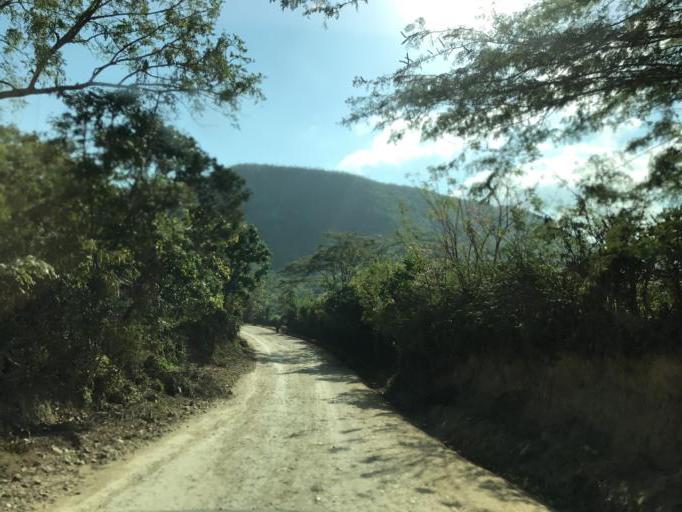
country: HT
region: Sud
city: Fond des Blancs
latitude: 18.2788
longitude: -73.1187
